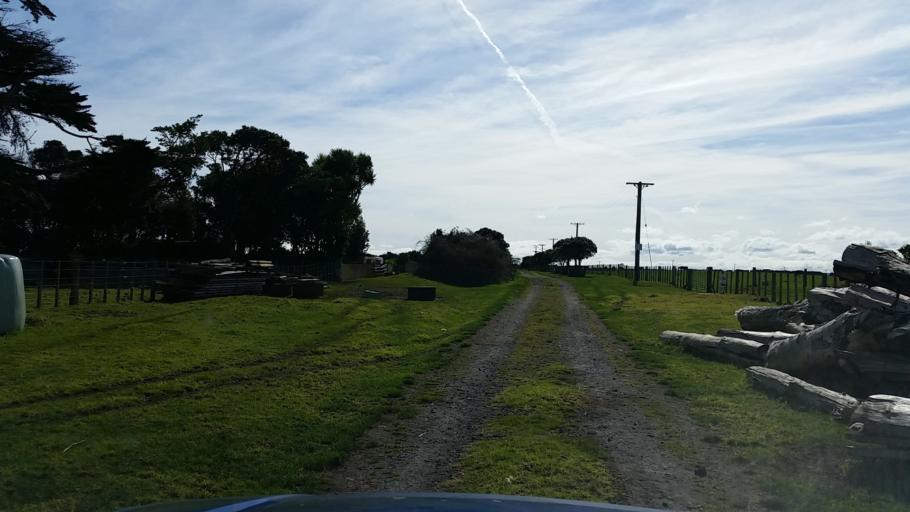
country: NZ
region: Taranaki
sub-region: South Taranaki District
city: Patea
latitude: -39.7696
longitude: 174.4937
